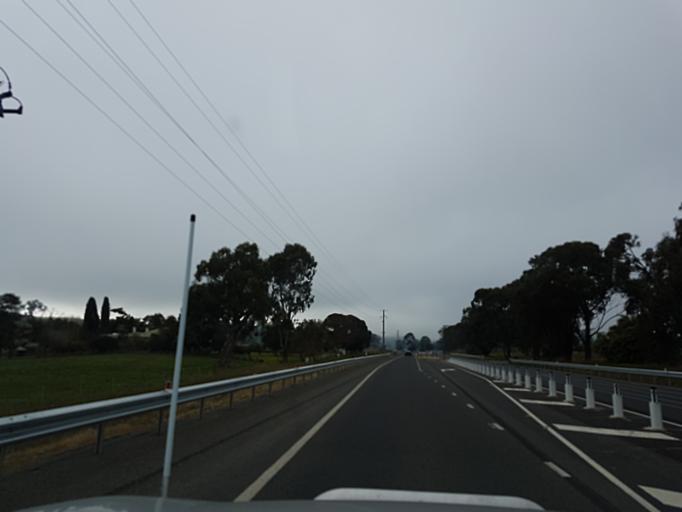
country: AU
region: Victoria
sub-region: Murrindindi
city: Alexandra
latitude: -37.2048
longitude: 145.4614
